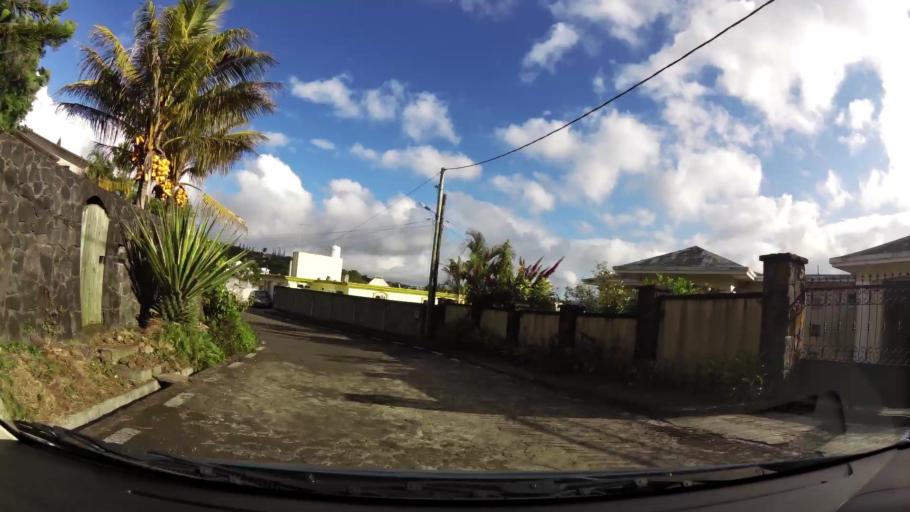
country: MU
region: Plaines Wilhems
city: Vacoas
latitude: -20.3085
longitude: 57.4966
